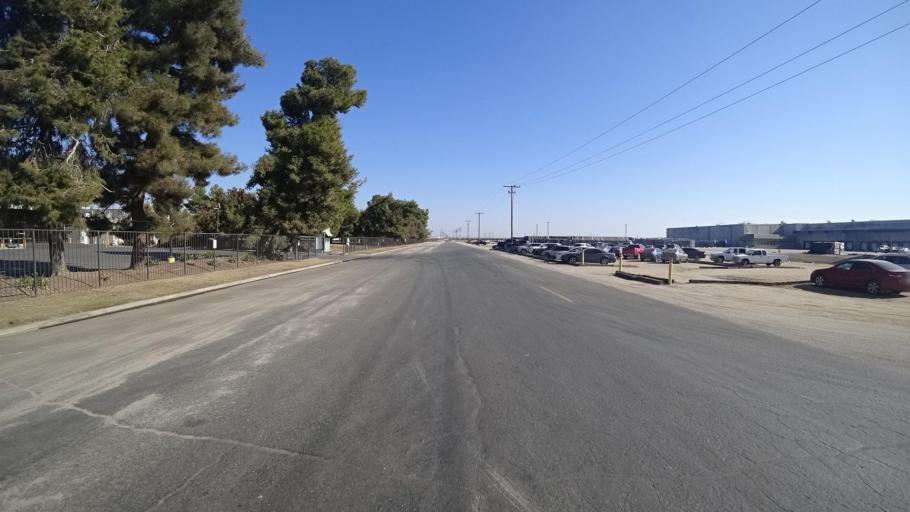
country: US
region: California
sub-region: Kern County
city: McFarland
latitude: 35.7034
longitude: -119.2280
